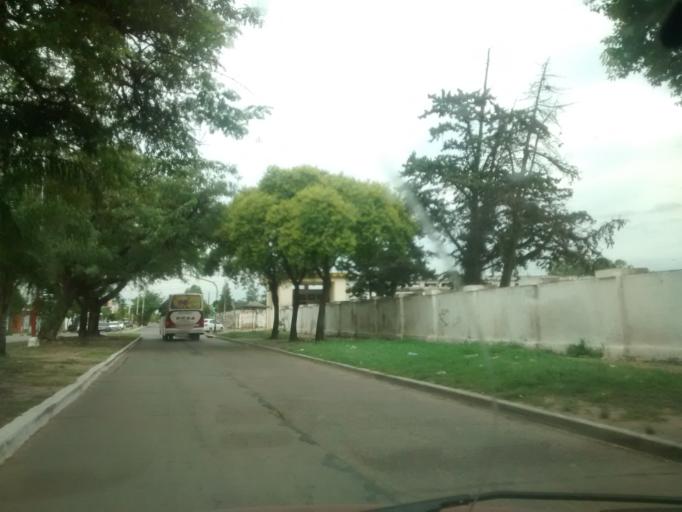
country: AR
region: Chaco
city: Resistencia
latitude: -27.4571
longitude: -59.0073
